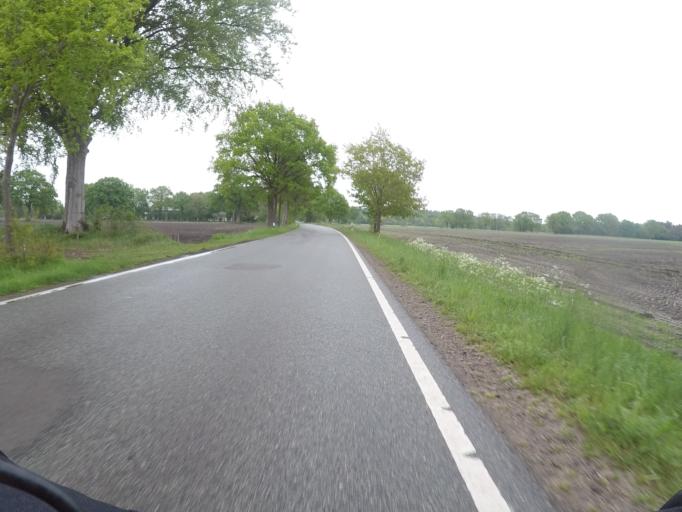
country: DE
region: Schleswig-Holstein
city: Heidmuhlen
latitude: 53.9706
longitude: 10.1322
